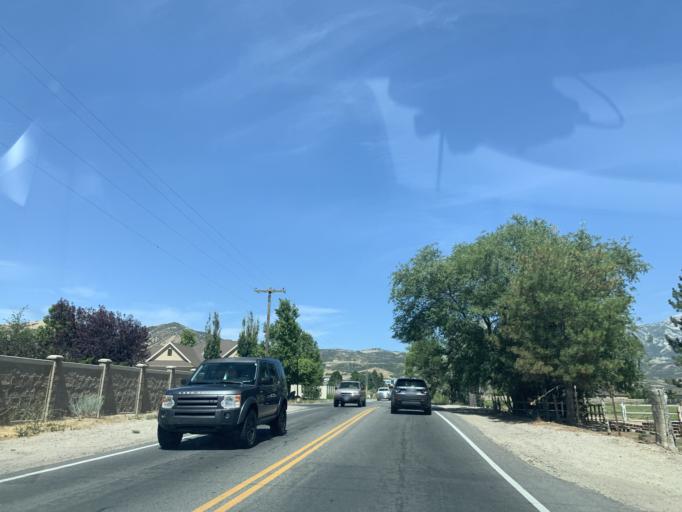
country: US
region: Utah
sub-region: Utah County
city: Lehi
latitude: 40.4254
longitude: -111.8305
